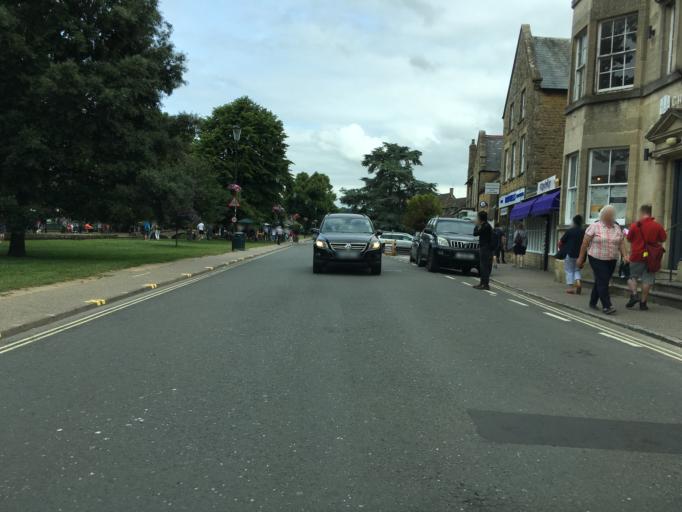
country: GB
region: England
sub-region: Gloucestershire
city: Bourton on the Water
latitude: 51.8839
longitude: -1.7569
